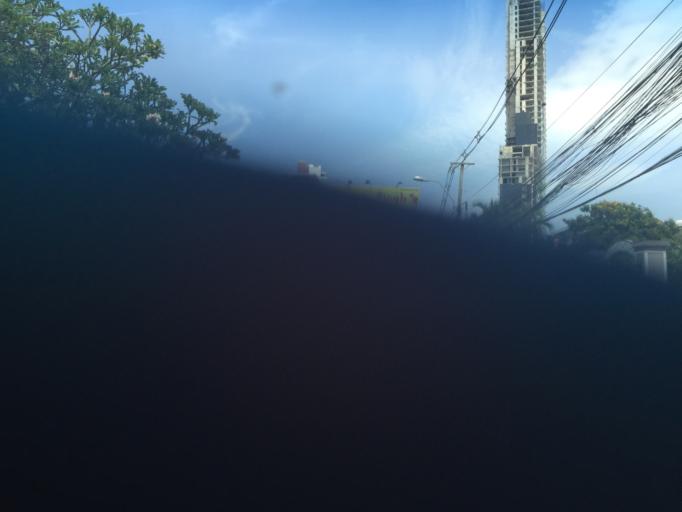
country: TH
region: Chon Buri
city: Phatthaya
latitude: 12.9247
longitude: 100.8691
